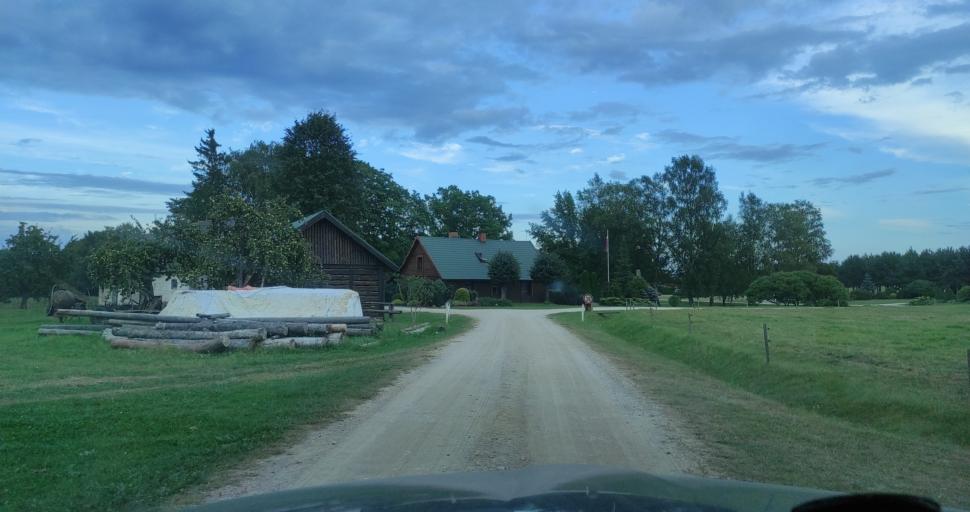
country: LV
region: Alsunga
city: Alsunga
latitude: 56.9336
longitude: 21.6439
